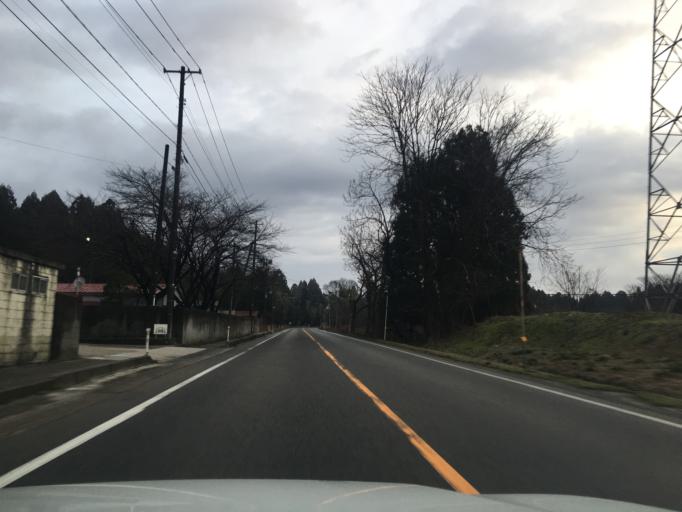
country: JP
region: Niigata
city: Murakami
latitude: 38.2914
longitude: 139.5279
